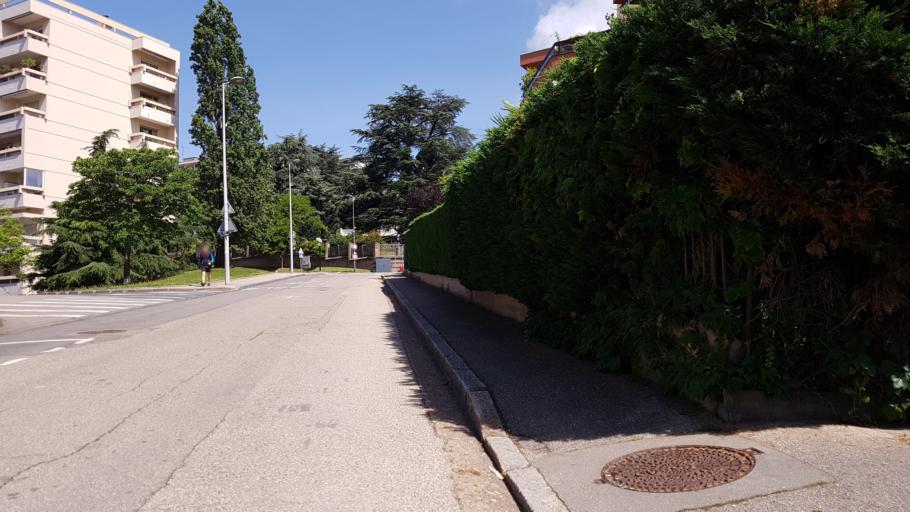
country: FR
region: Rhone-Alpes
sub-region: Departement du Rhone
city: Caluire-et-Cuire
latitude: 45.7920
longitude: 4.8540
